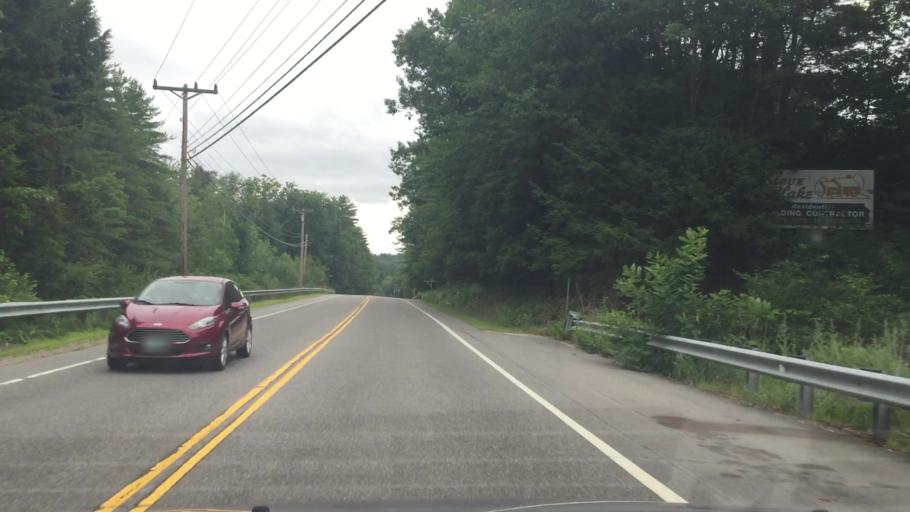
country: US
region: New Hampshire
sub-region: Belknap County
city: Meredith
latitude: 43.6198
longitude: -71.5705
